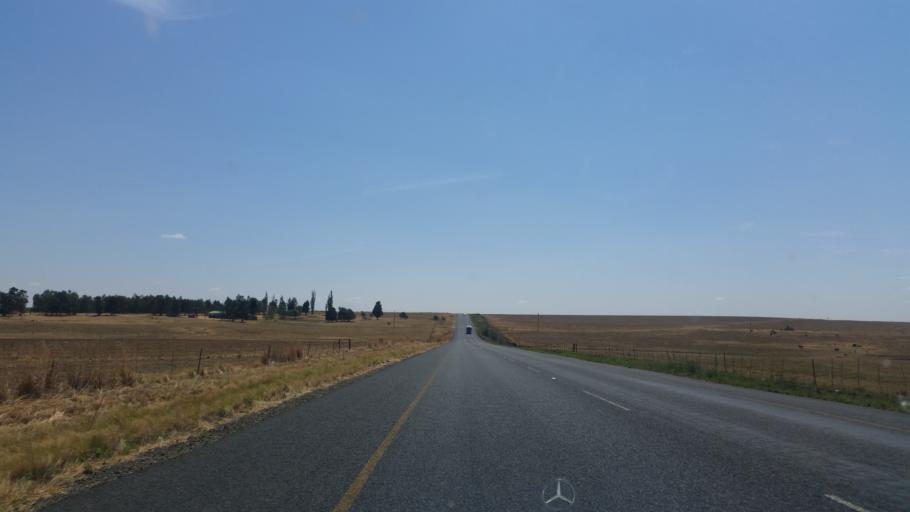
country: ZA
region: Orange Free State
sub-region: Thabo Mofutsanyana District Municipality
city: Phuthaditjhaba
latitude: -28.1947
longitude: 28.6870
